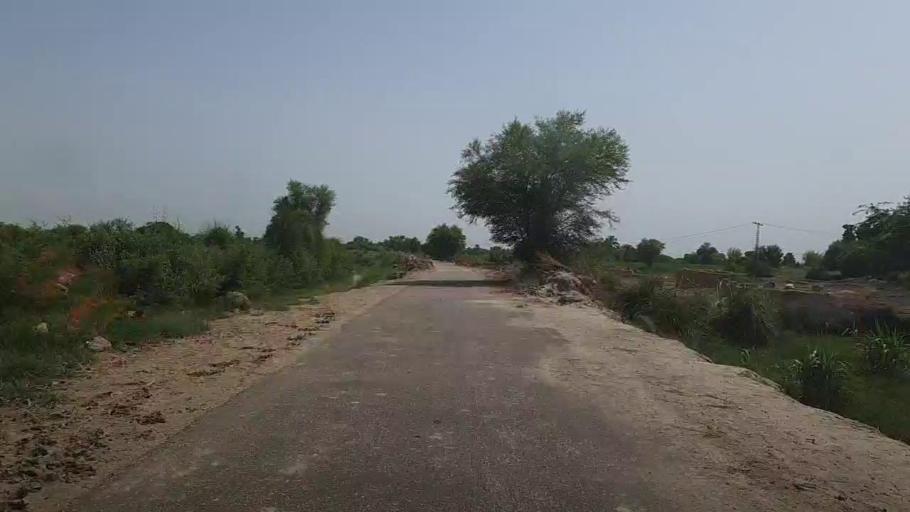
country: PK
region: Sindh
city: Pad Idan
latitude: 26.8254
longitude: 68.3284
